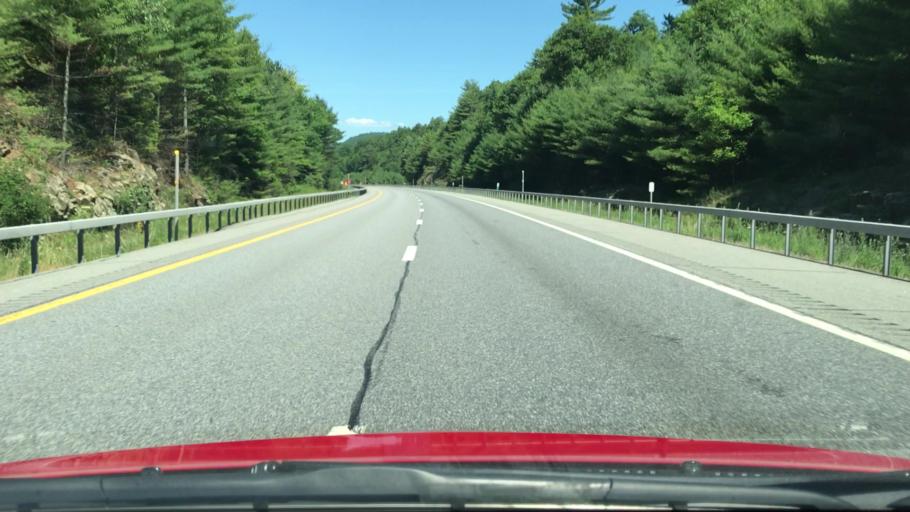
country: US
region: New York
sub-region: Warren County
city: Warrensburg
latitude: 43.4727
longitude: -73.7482
